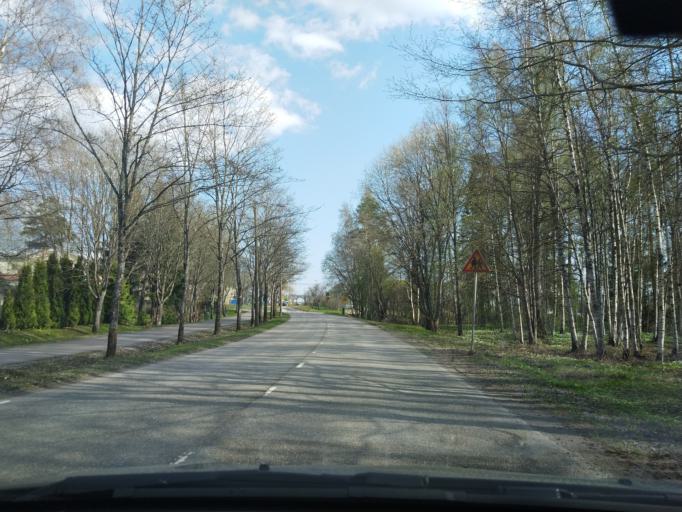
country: FI
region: Uusimaa
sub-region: Helsinki
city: Lohja
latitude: 60.1808
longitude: 23.9896
